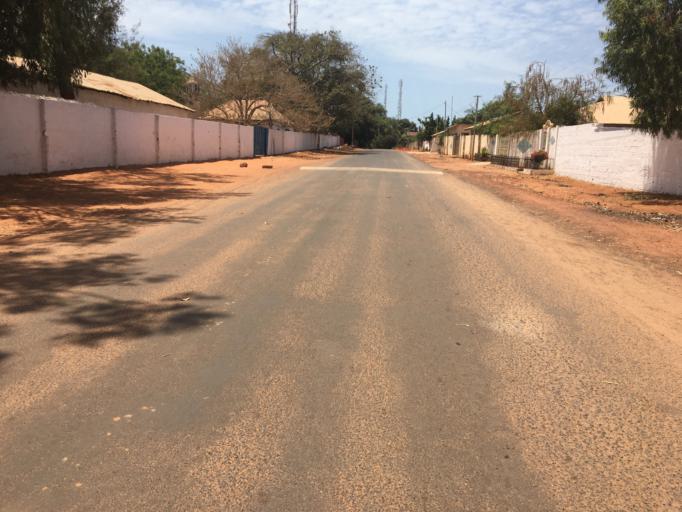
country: GM
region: Banjul
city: Bakau
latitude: 13.4722
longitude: -16.6844
